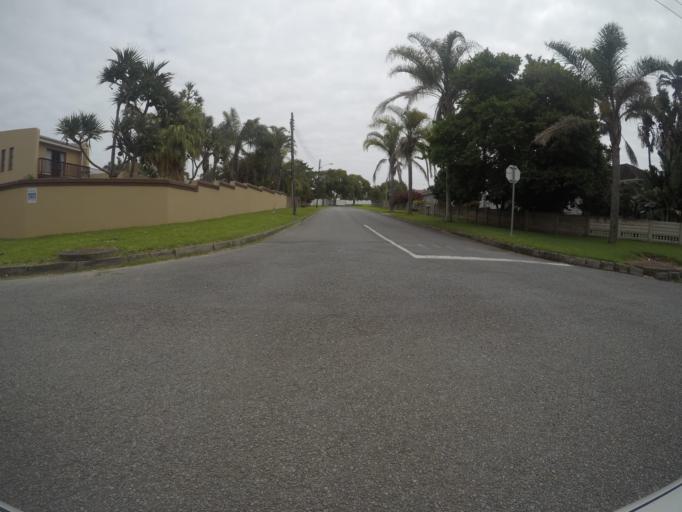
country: ZA
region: Eastern Cape
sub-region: Buffalo City Metropolitan Municipality
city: East London
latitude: -32.9742
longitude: 27.9424
